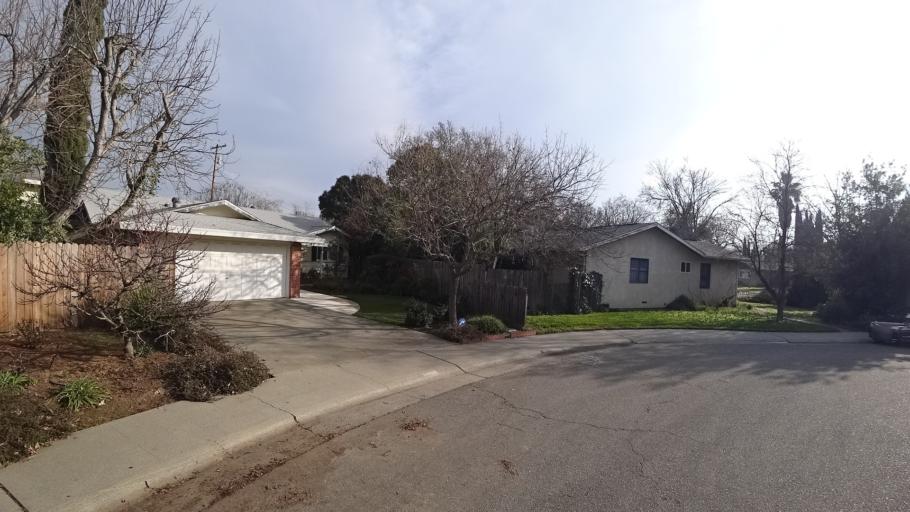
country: US
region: California
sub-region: Yolo County
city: Davis
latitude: 38.5596
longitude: -121.7267
